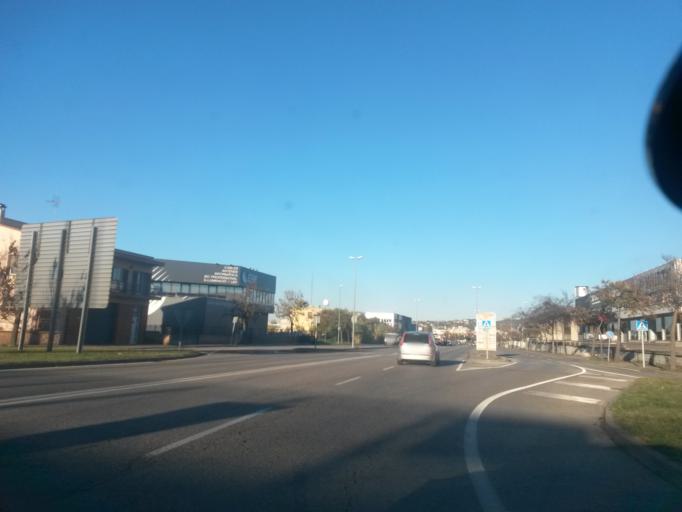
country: ES
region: Catalonia
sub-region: Provincia de Girona
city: Salt
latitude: 41.9601
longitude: 2.8030
